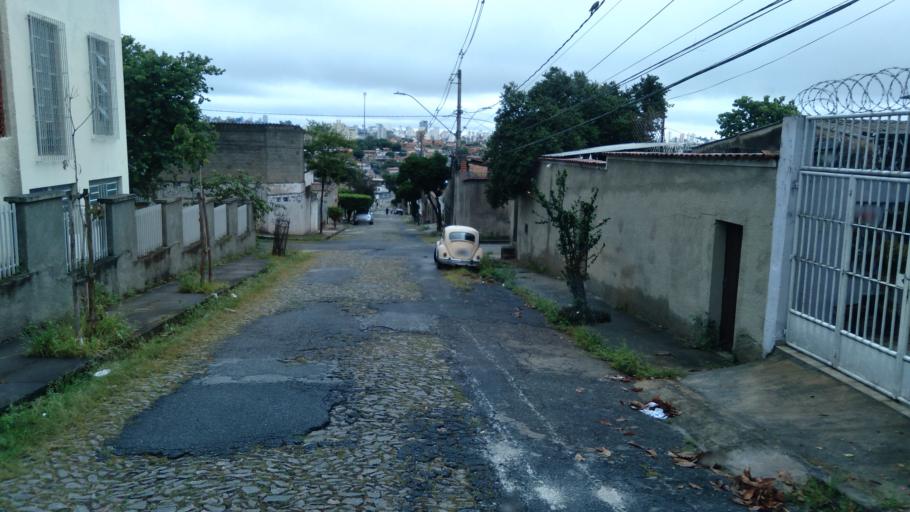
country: BR
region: Minas Gerais
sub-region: Belo Horizonte
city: Belo Horizonte
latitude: -19.9167
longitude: -43.8985
